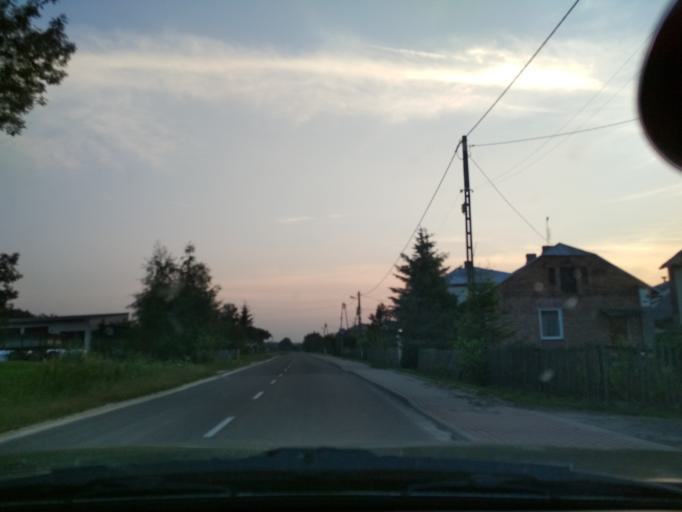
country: PL
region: Silesian Voivodeship
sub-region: Powiat zawiercianski
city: Pilica
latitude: 50.4710
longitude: 19.7385
